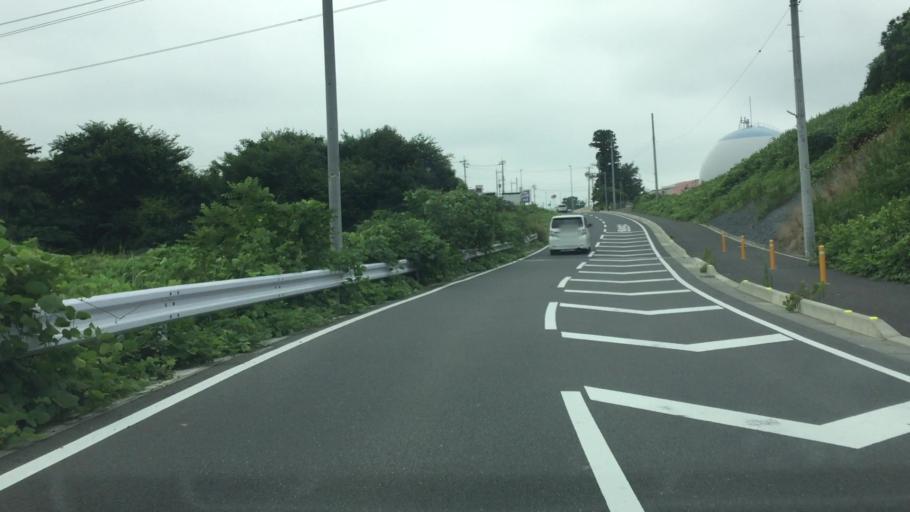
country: JP
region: Chiba
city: Abiko
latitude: 35.8368
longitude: 140.0169
